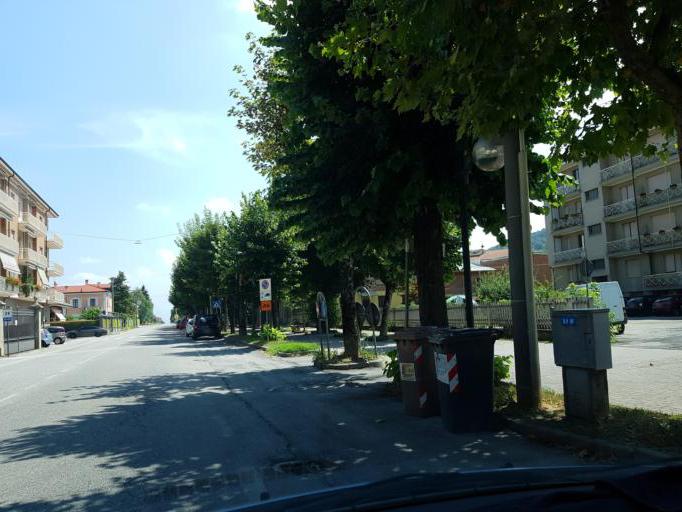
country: IT
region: Piedmont
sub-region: Provincia di Cuneo
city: Dronero
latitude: 44.4622
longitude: 7.3697
